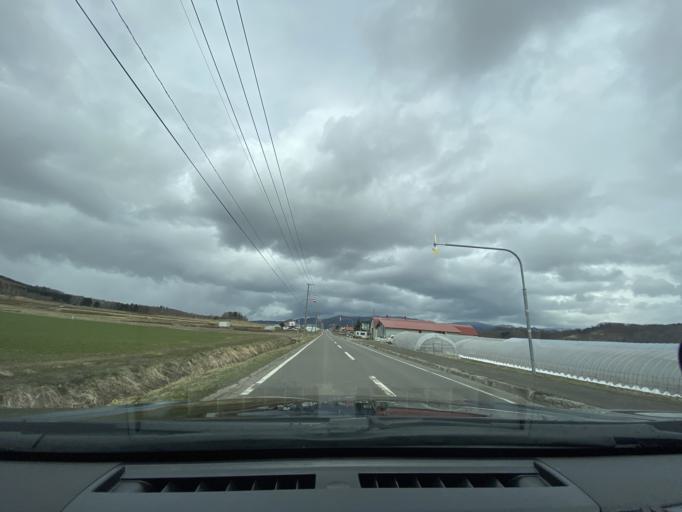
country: JP
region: Hokkaido
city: Nayoro
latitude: 44.0971
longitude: 142.4745
